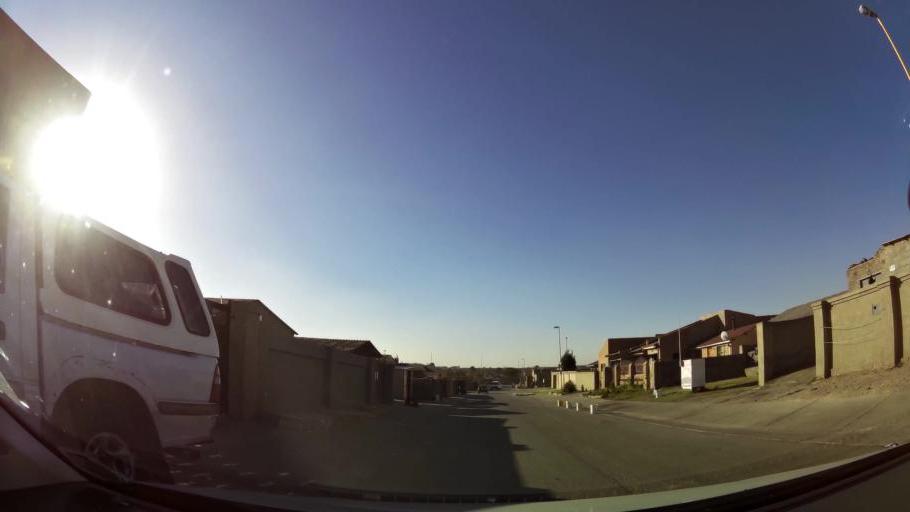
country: ZA
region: Gauteng
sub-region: Ekurhuleni Metropolitan Municipality
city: Tembisa
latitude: -26.0177
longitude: 28.2216
